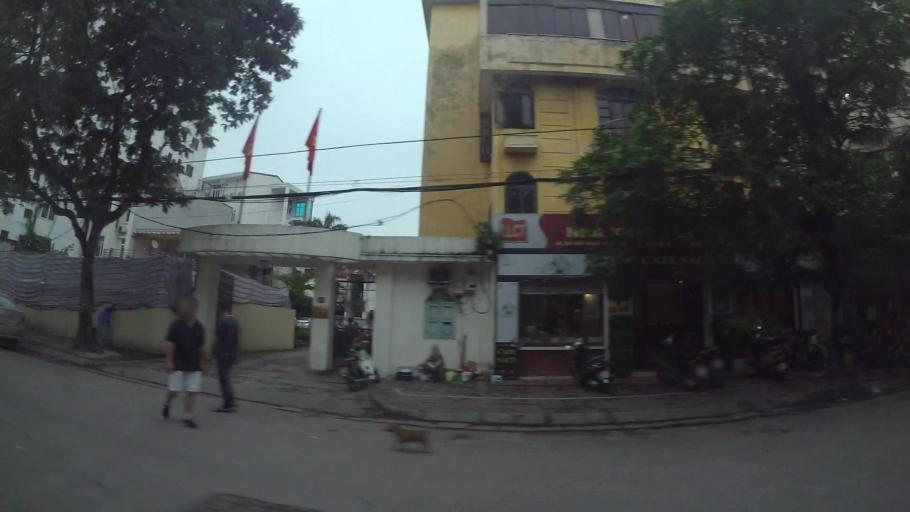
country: VN
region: Ha Noi
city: Hanoi
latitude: 21.0268
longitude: 105.8365
